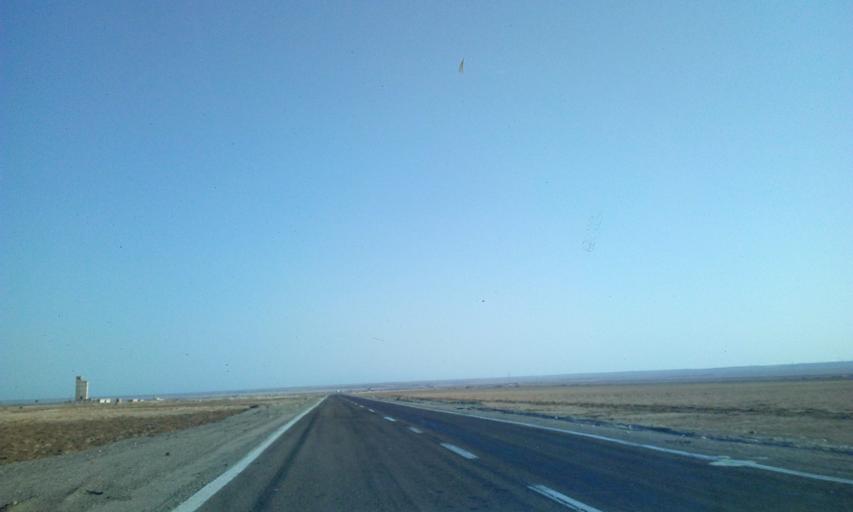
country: EG
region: South Sinai
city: Tor
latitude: 28.5991
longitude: 32.8627
